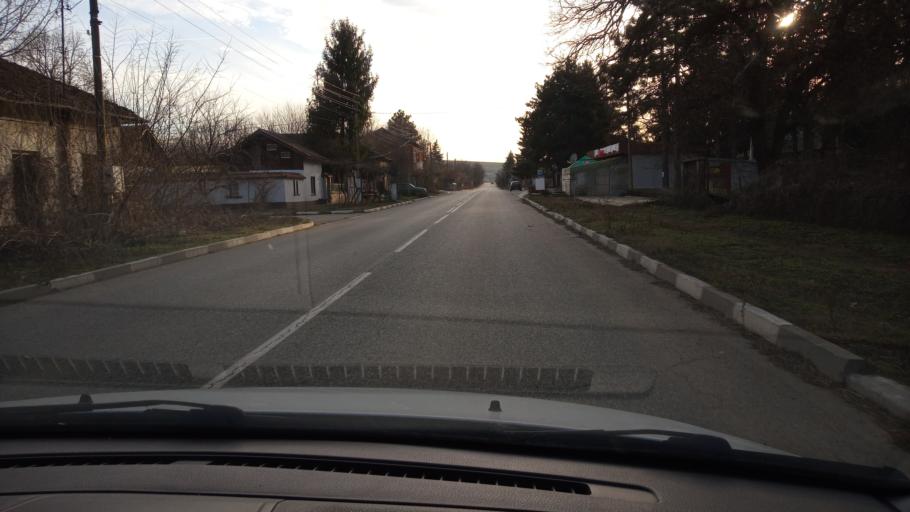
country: BG
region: Pleven
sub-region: Obshtina Pleven
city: Slavyanovo
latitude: 43.5544
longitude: 24.8655
